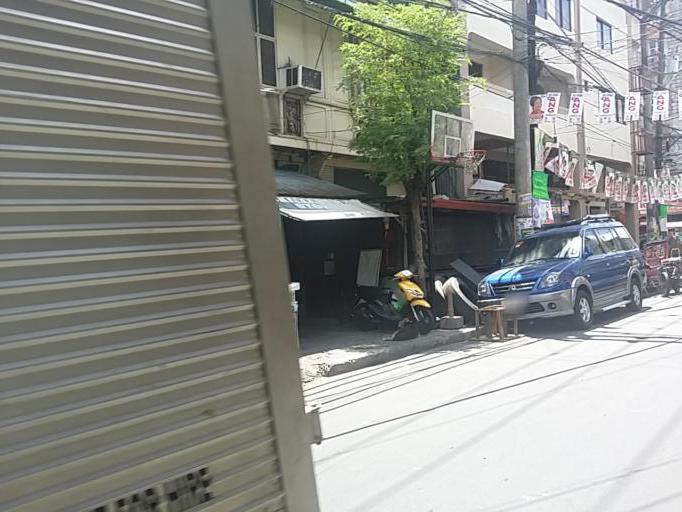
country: PH
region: Metro Manila
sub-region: City of Manila
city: Quiapo
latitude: 14.6007
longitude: 120.9870
